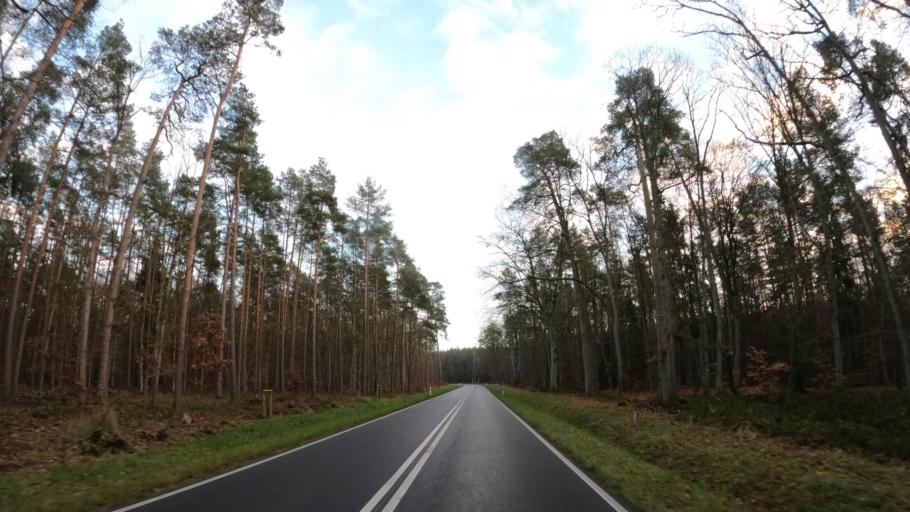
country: PL
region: West Pomeranian Voivodeship
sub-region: Powiat policki
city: Nowe Warpno
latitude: 53.6689
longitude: 14.4181
